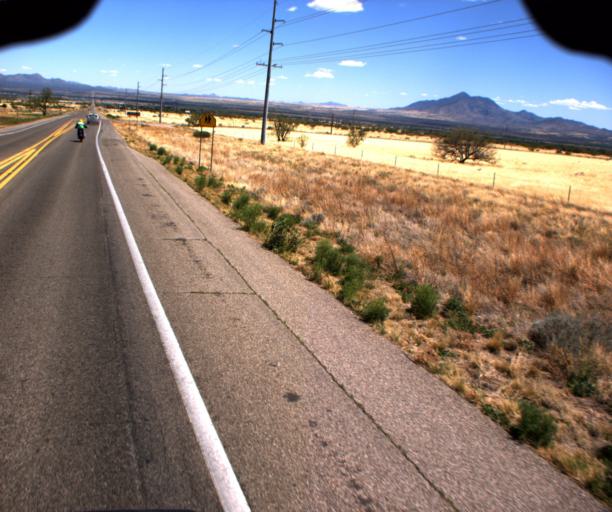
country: US
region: Arizona
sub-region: Cochise County
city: Sierra Vista Southeast
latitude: 31.3799
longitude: -110.2092
